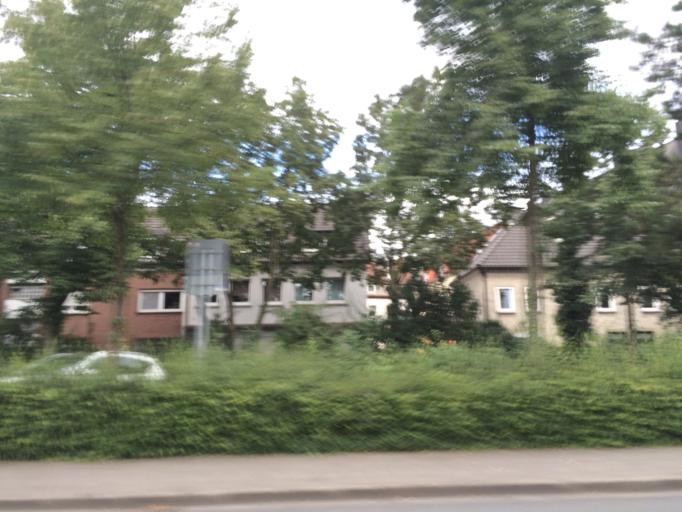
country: DE
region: North Rhine-Westphalia
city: Dorsten
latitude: 51.6618
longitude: 6.9621
